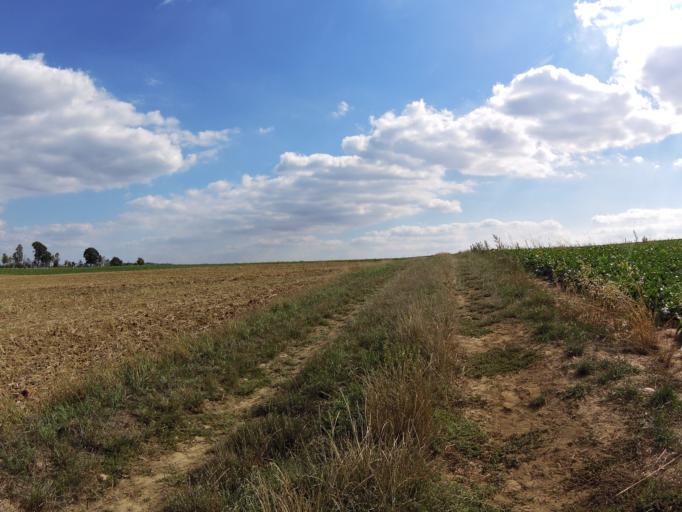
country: DE
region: Bavaria
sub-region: Regierungsbezirk Unterfranken
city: Hettstadt
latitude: 49.7927
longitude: 9.8196
